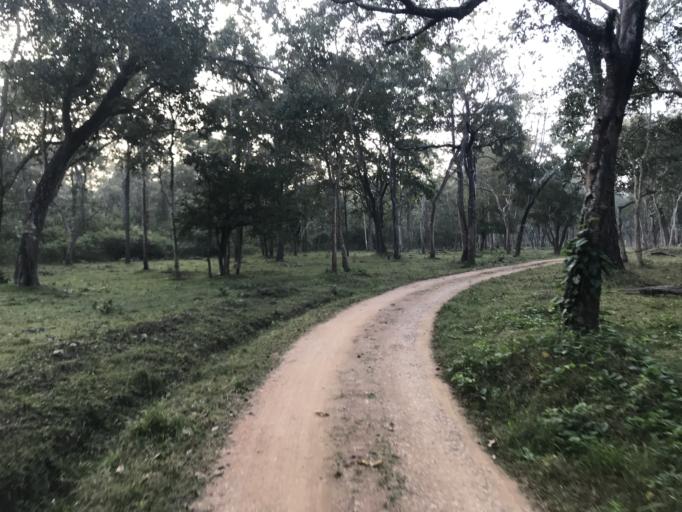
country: IN
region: Karnataka
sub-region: Mysore
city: Heggadadevankote
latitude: 11.9964
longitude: 76.2174
